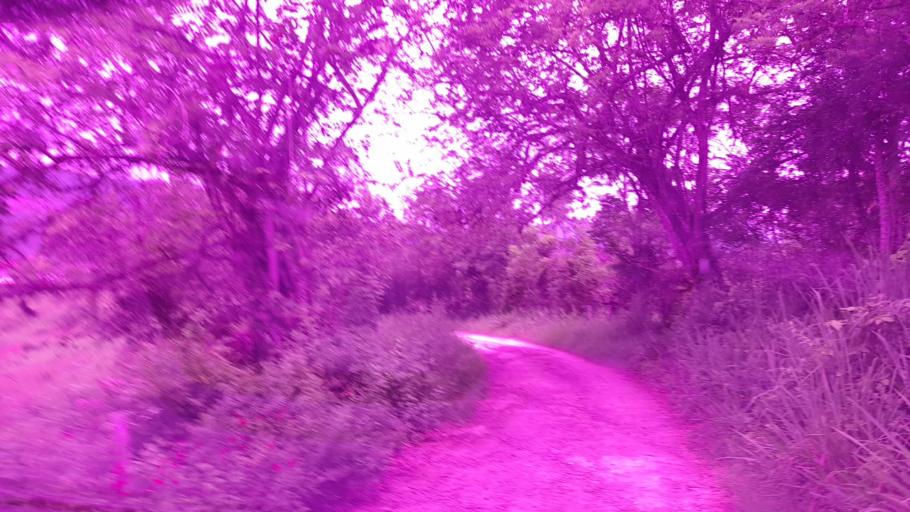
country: CO
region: Valle del Cauca
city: Andalucia
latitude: 4.1680
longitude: -76.0923
